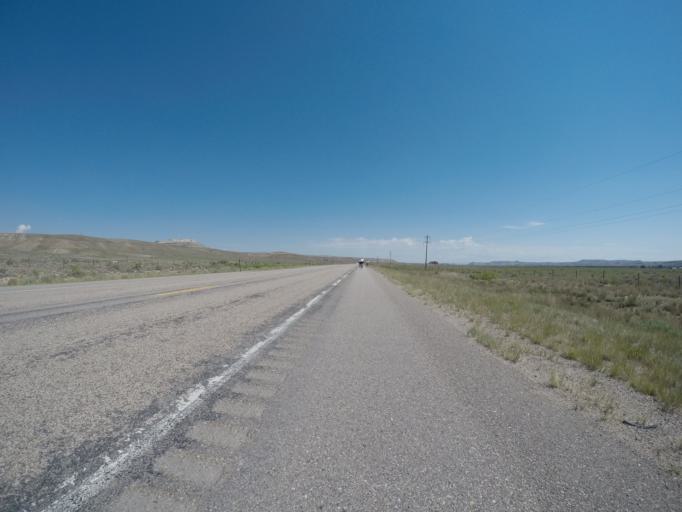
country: US
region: Wyoming
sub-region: Sublette County
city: Marbleton
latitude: 42.3629
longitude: -110.1532
